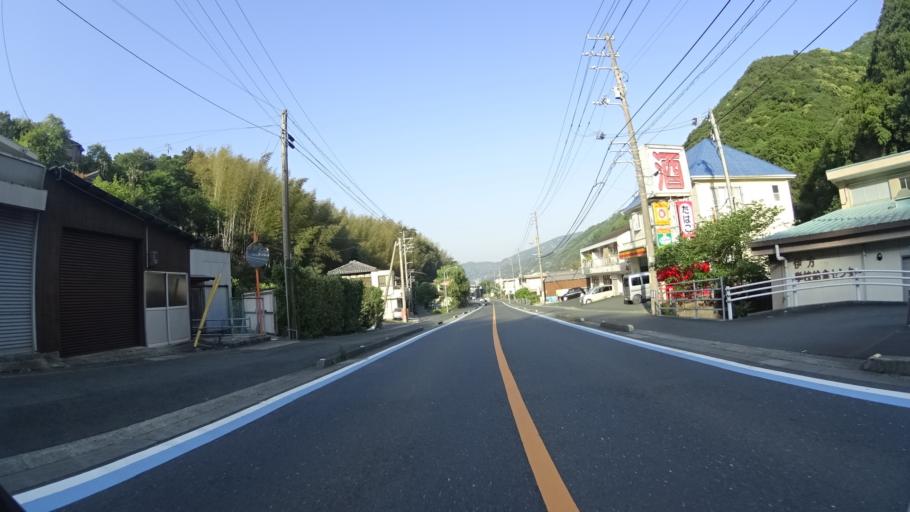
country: JP
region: Ehime
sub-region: Nishiuwa-gun
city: Ikata-cho
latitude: 33.4944
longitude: 132.3667
